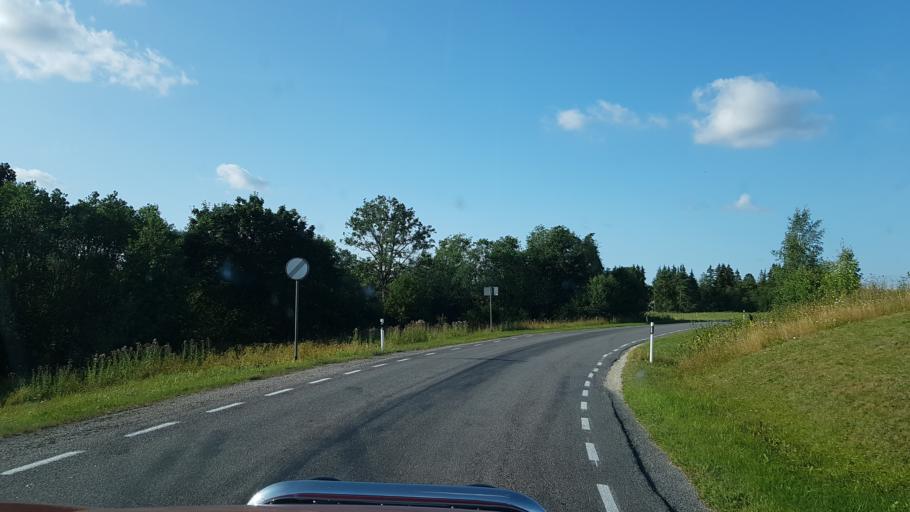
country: EE
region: Jaervamaa
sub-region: Jaerva-Jaani vald
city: Jarva-Jaani
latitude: 59.1207
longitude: 25.6594
